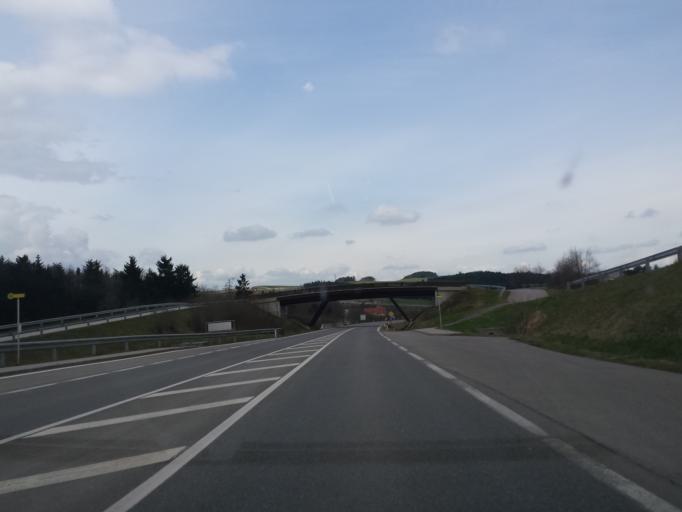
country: AT
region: Lower Austria
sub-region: Politischer Bezirk Krems
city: Jaidhof
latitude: 48.5261
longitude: 15.4380
